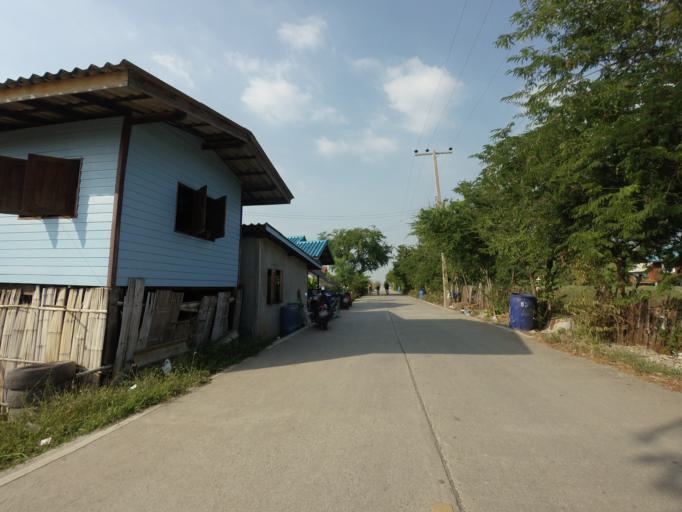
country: TH
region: Samut Sakhon
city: Samut Sakhon
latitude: 13.4994
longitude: 100.3282
